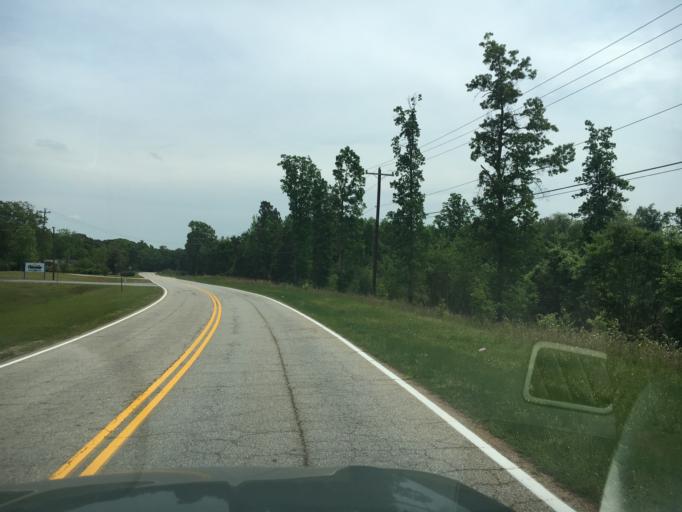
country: US
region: South Carolina
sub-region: Spartanburg County
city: Fairforest
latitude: 34.9753
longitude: -82.0150
